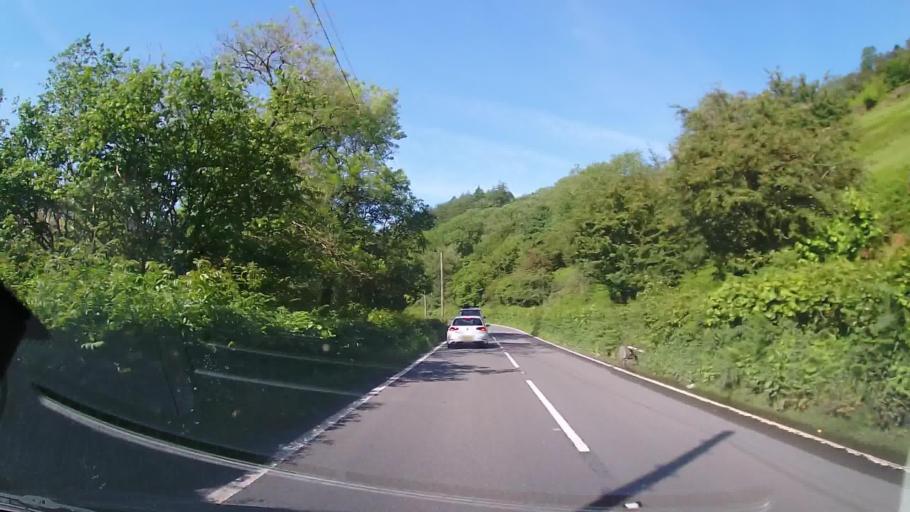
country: GB
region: Wales
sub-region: Gwynedd
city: Bala
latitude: 52.7030
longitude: -3.6136
